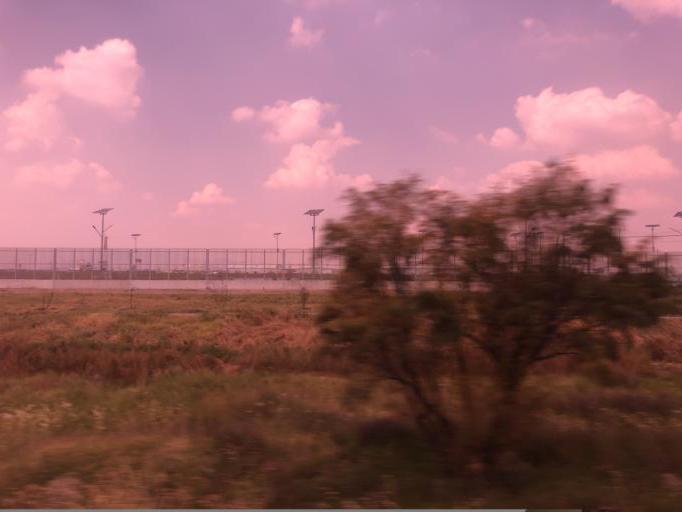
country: MX
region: Mexico
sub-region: Ciudad Nezahualcoyotl
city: Poligonos
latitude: 19.4770
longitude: -98.9840
